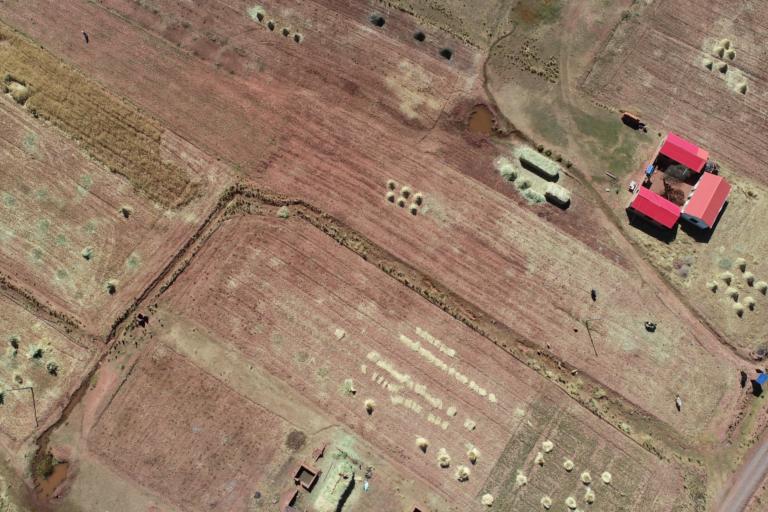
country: BO
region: La Paz
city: Tiahuanaco
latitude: -16.5932
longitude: -68.7575
